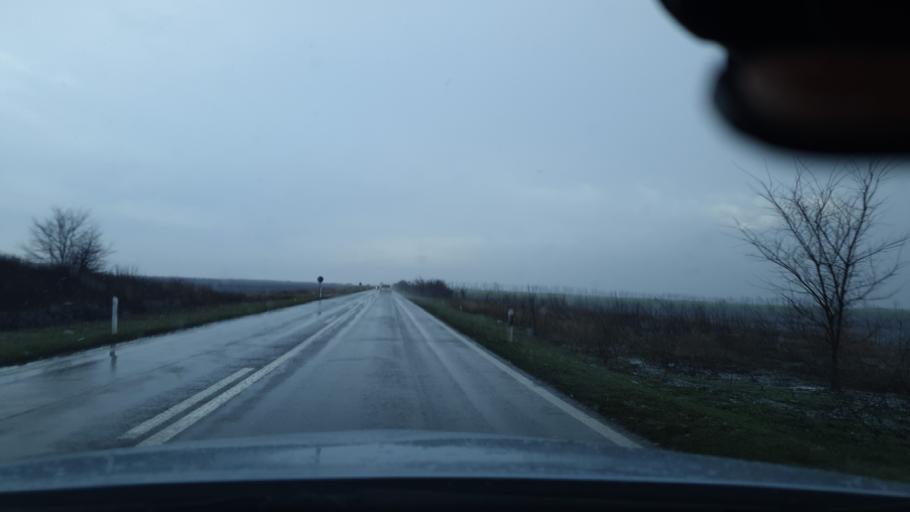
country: RS
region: Autonomna Pokrajina Vojvodina
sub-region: Juznobanatski Okrug
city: Pancevo
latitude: 44.8494
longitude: 20.7747
